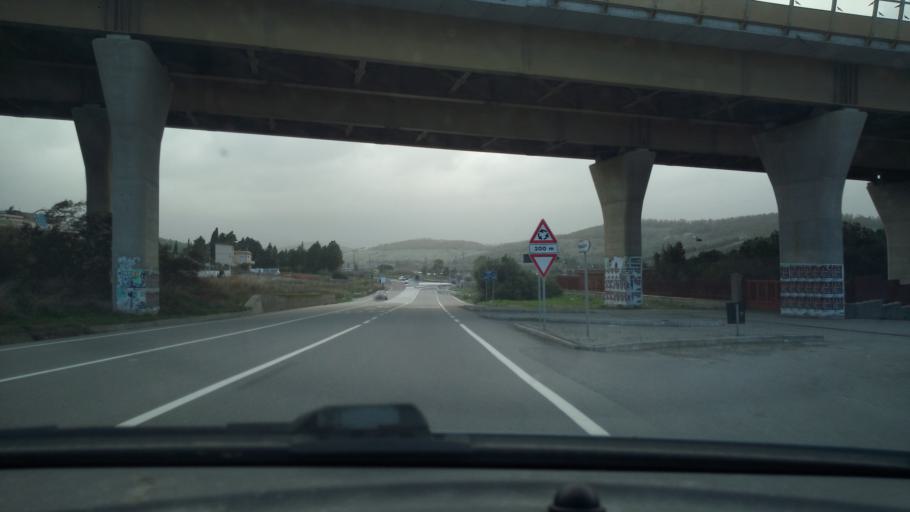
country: IT
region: Calabria
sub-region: Provincia di Catanzaro
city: Barone
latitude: 38.8610
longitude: 16.6308
